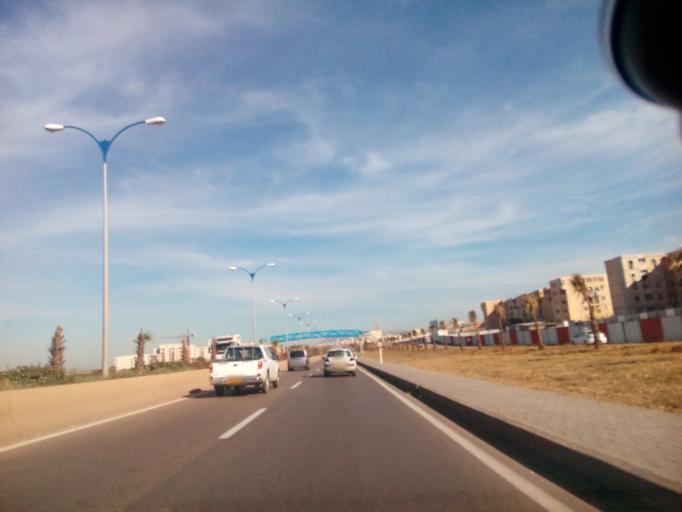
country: DZ
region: Mostaganem
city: Mostaganem
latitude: 35.8992
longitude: 0.0628
